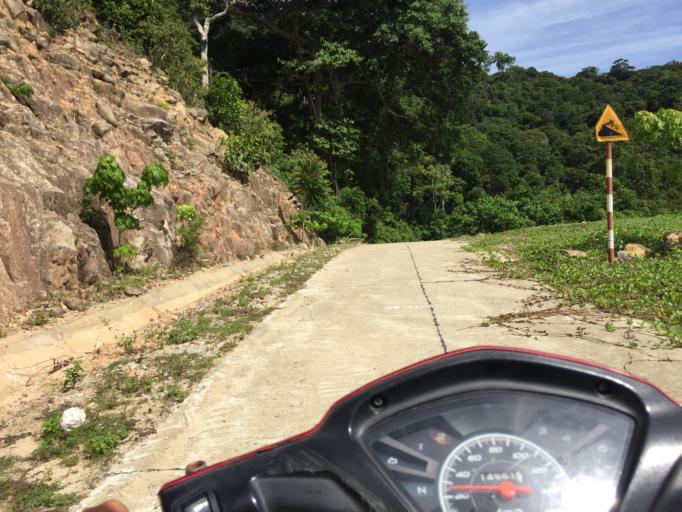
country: VN
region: Quang Nam
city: Hoi An
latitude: 15.9487
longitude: 108.5309
